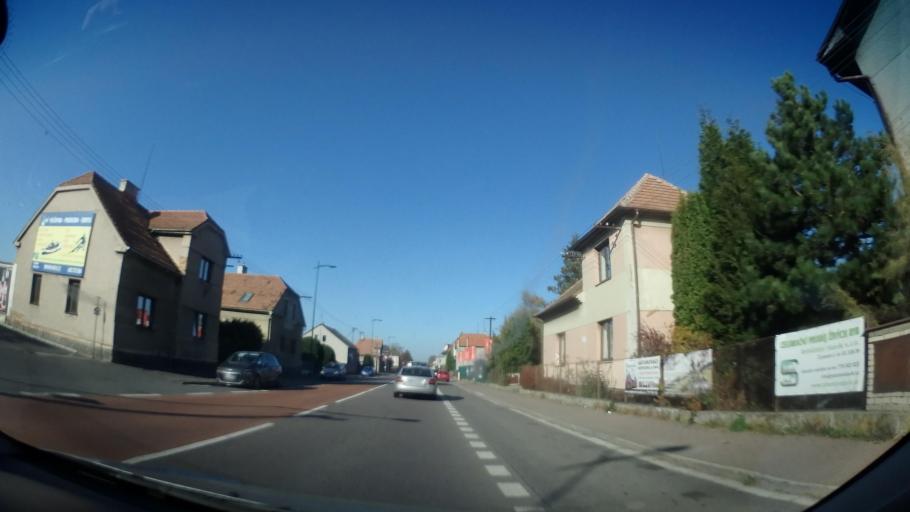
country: CZ
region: Pardubicky
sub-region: Okres Chrudim
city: Slatinany
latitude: 49.9141
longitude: 15.8171
